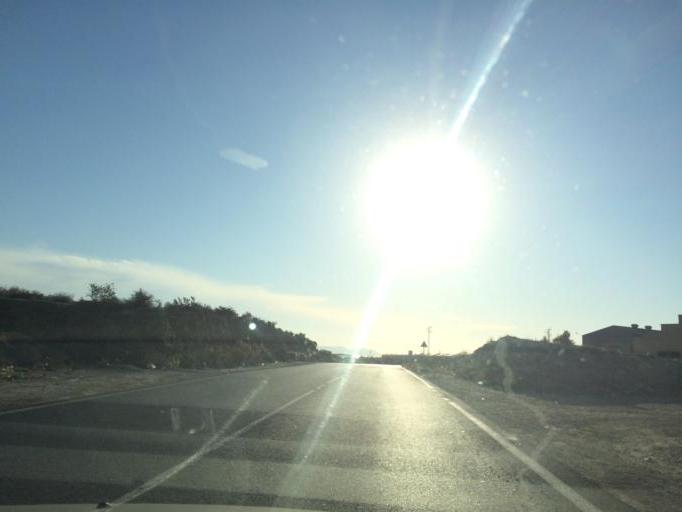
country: ES
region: Andalusia
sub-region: Provincia de Almeria
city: Viator
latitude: 36.8859
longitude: -2.4151
